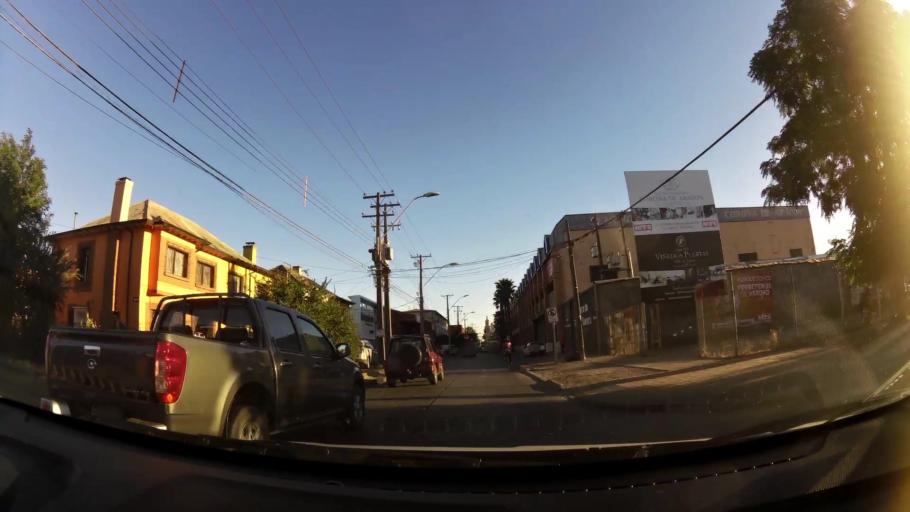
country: CL
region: Maule
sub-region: Provincia de Curico
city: Curico
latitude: -34.9801
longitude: -71.2408
